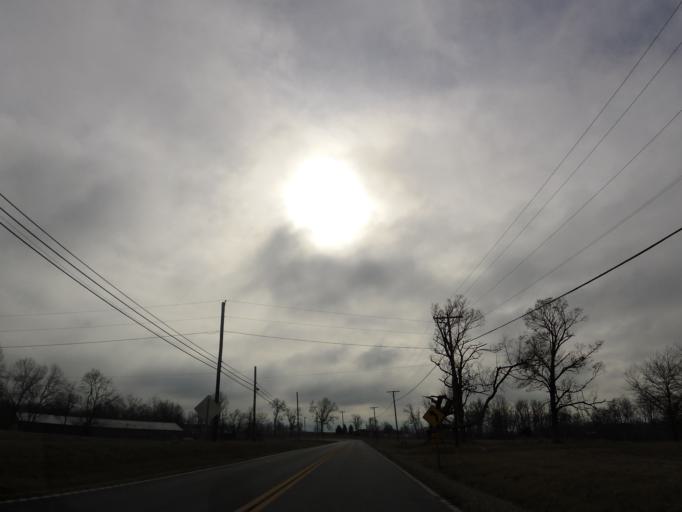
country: US
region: Kentucky
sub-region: Trimble County
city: Bedford
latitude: 38.6148
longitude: -85.3230
